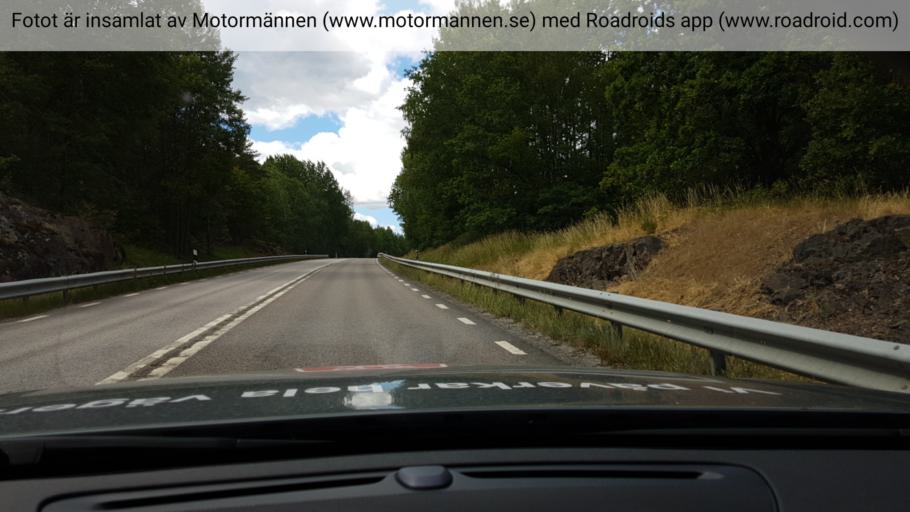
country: SE
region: Stockholm
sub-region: Osterakers Kommun
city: Akersberga
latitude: 59.4269
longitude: 18.2503
